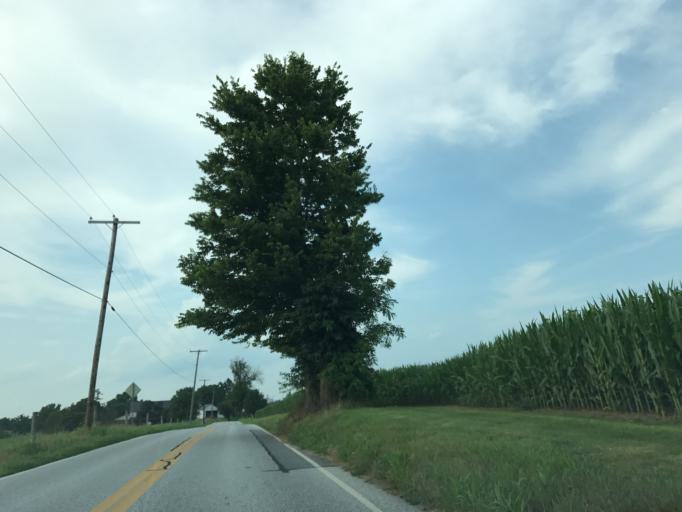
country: US
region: Pennsylvania
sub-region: Lancaster County
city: Mount Joy
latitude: 40.0961
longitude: -76.5350
